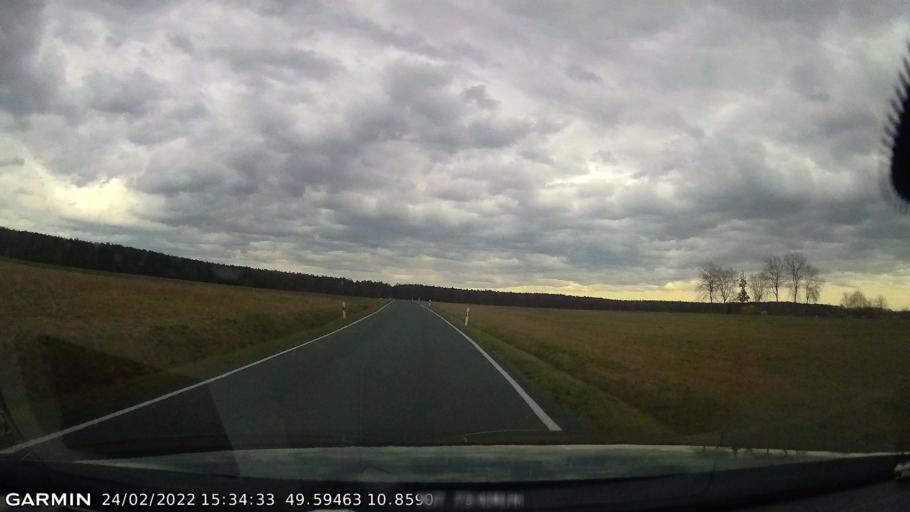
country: DE
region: Bavaria
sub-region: Regierungsbezirk Mittelfranken
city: Herzogenaurach
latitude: 49.5946
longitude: 10.8593
